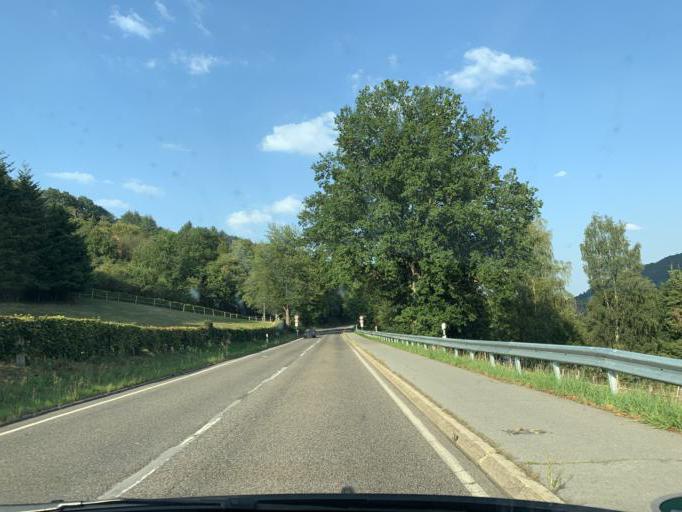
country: DE
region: North Rhine-Westphalia
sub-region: Regierungsbezirk Koln
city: Simmerath
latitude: 50.6224
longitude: 6.3760
